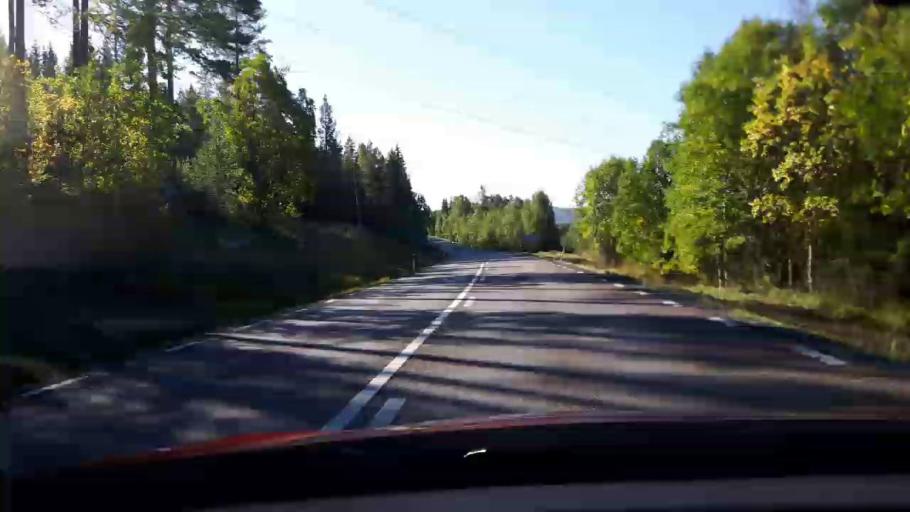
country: SE
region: Jaemtland
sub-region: OEstersunds Kommun
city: Brunflo
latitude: 62.9685
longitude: 15.0207
